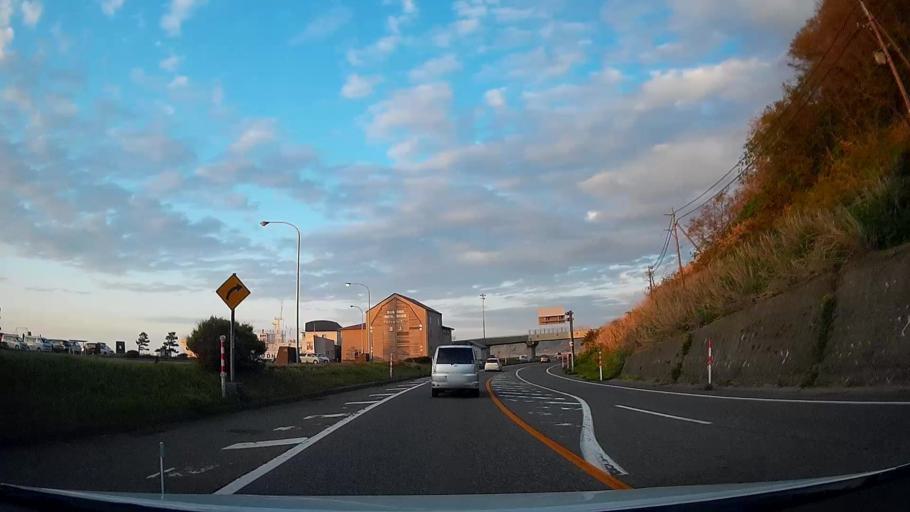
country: JP
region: Niigata
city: Itoigawa
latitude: 37.1137
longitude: 138.0050
